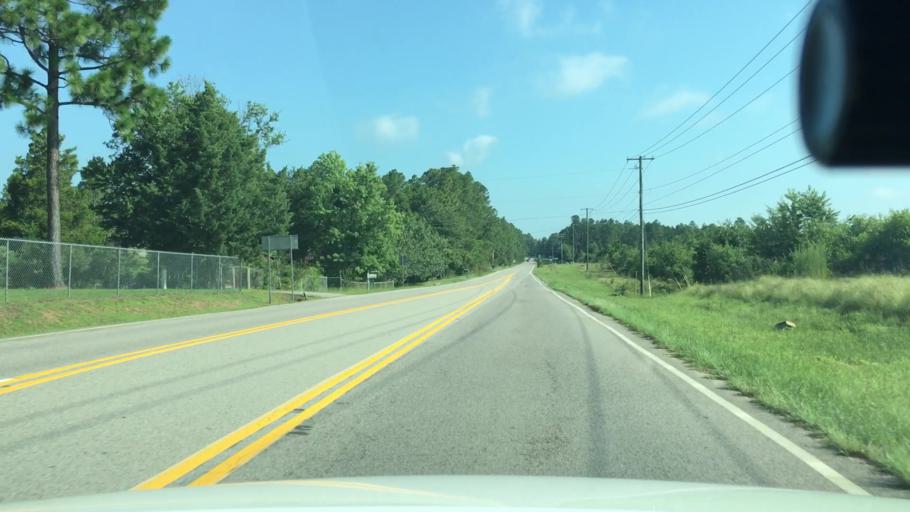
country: US
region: South Carolina
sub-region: Aiken County
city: Graniteville
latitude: 33.5852
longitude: -81.8362
